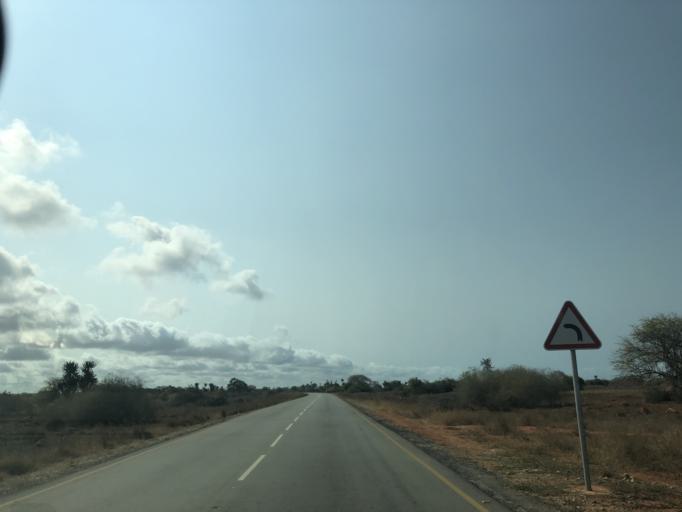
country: AO
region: Luanda
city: Luanda
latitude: -9.7046
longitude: 13.2159
